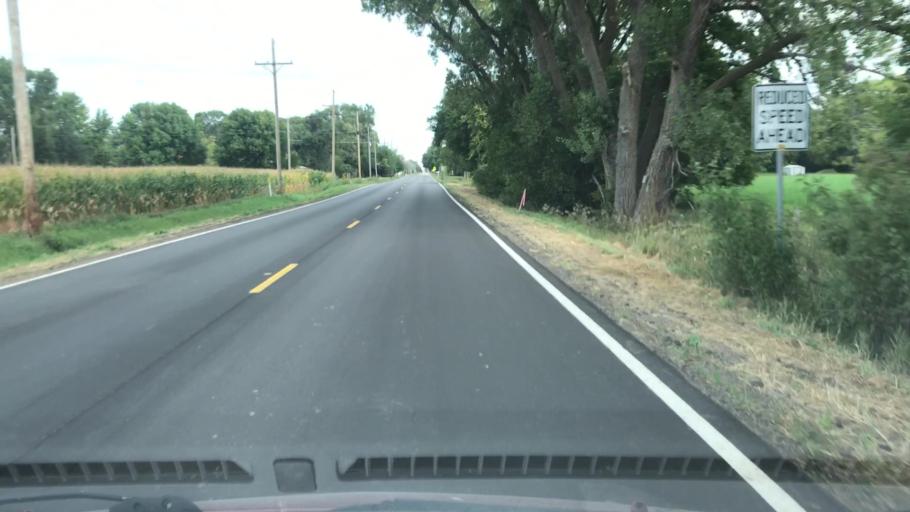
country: US
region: Nebraska
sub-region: Hall County
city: Grand Island
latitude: 40.9265
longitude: -98.3015
